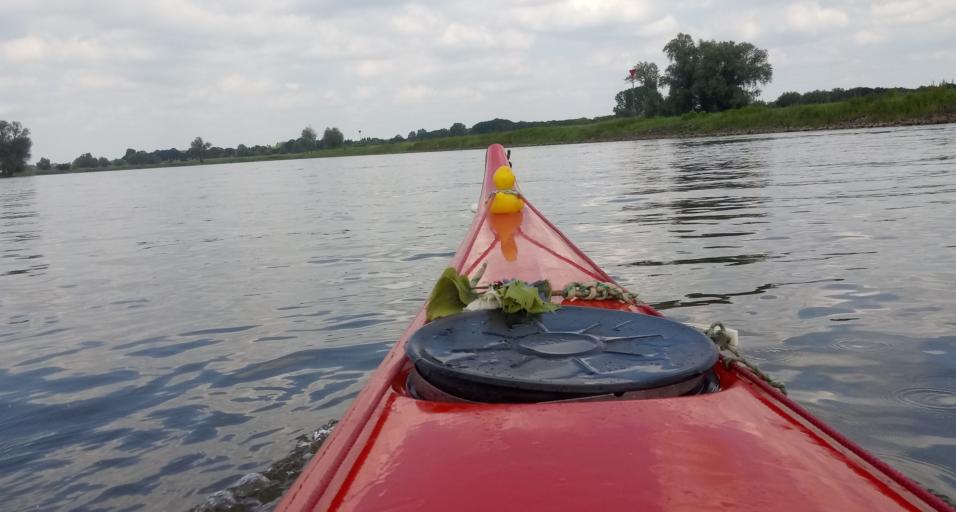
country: NL
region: Gelderland
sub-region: Gemeente Zutphen
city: Zutphen
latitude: 52.1660
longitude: 6.1891
